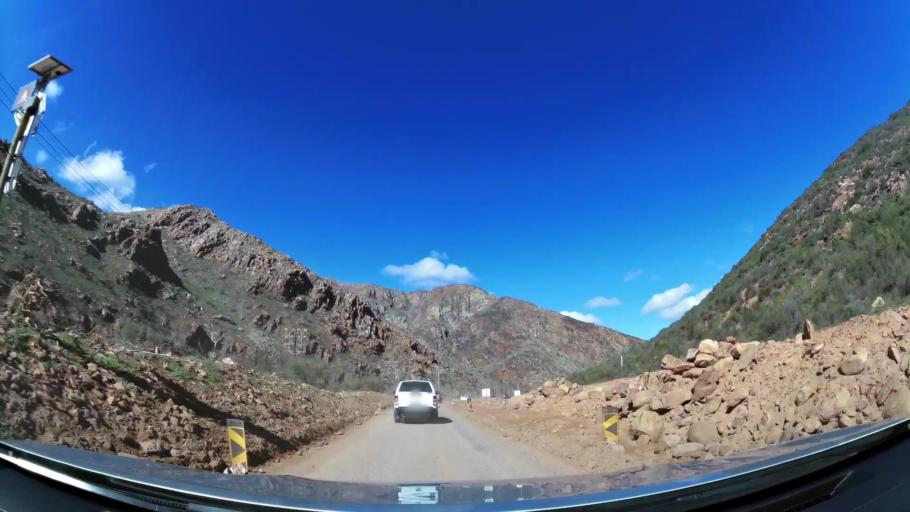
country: ZA
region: Western Cape
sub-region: Cape Winelands District Municipality
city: Ashton
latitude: -33.8049
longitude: 20.0937
